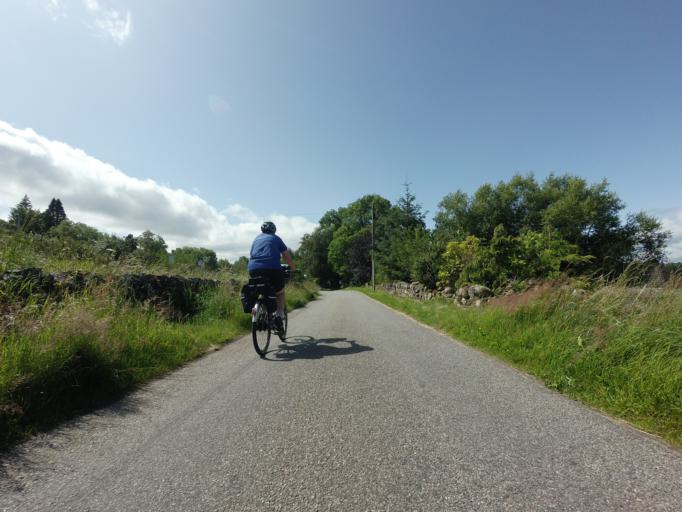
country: GB
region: Scotland
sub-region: Highland
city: Nairn
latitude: 57.5028
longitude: -3.9974
